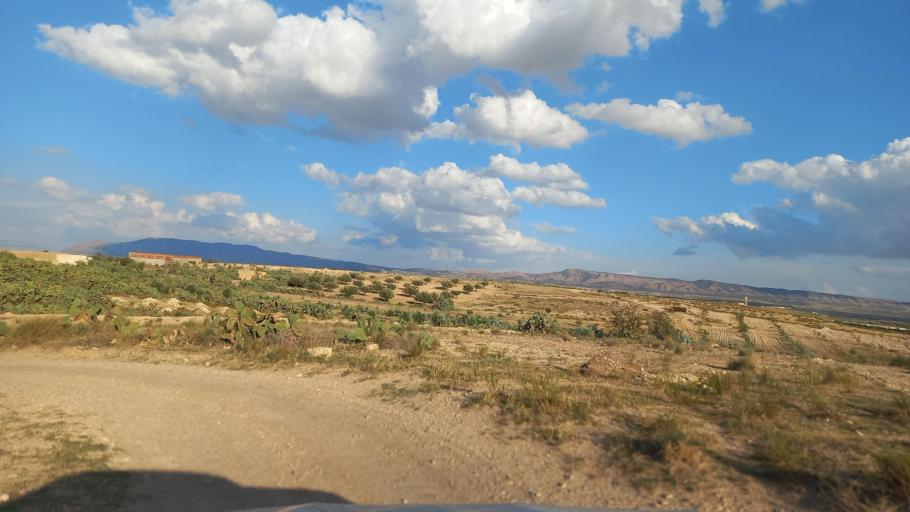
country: TN
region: Al Qasrayn
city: Sbiba
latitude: 35.3907
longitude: 9.0533
